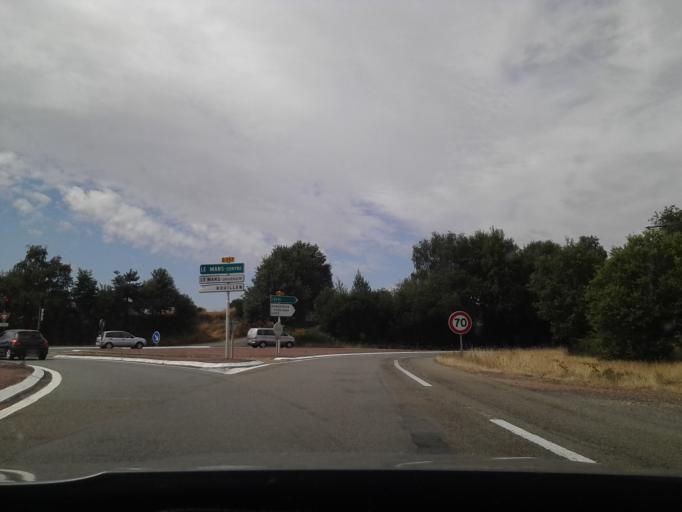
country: FR
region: Pays de la Loire
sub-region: Departement de la Sarthe
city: Trange
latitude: 48.0197
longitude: 0.1249
